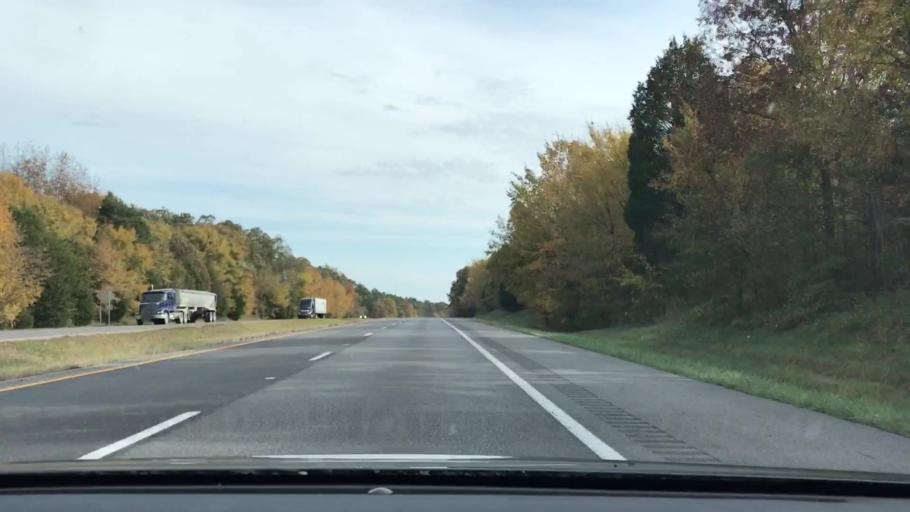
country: US
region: Kentucky
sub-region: Graves County
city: Mayfield
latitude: 36.7840
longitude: -88.5500
